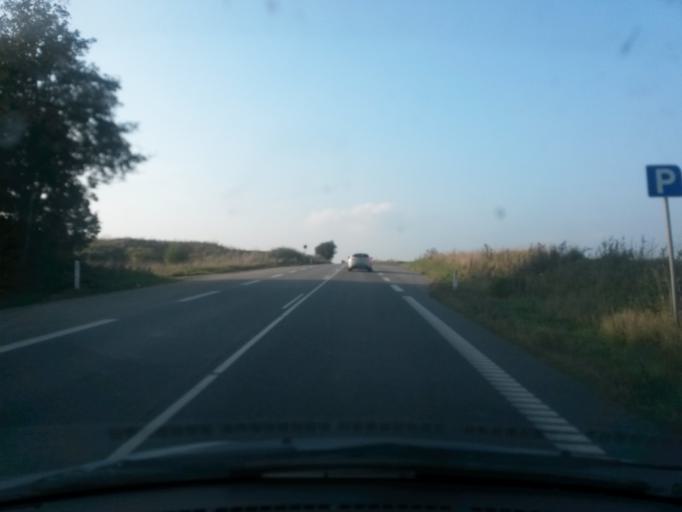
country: DK
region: Central Jutland
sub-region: Syddjurs Kommune
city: Hornslet
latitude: 56.3752
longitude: 10.3095
